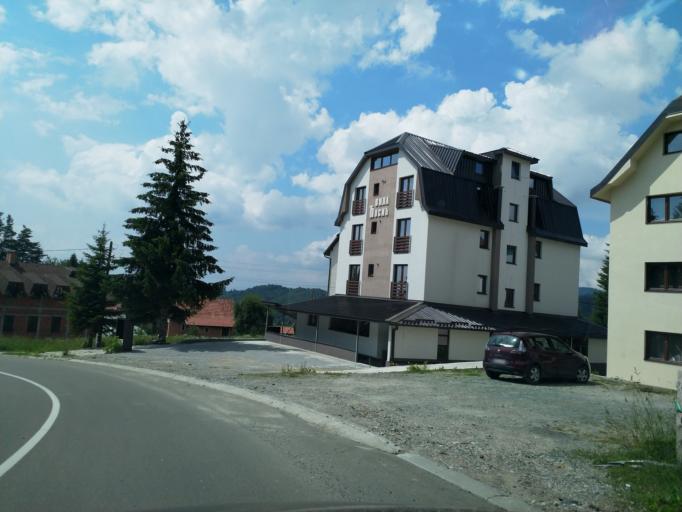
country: RS
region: Central Serbia
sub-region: Raski Okrug
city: Raska
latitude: 43.2759
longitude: 20.7638
